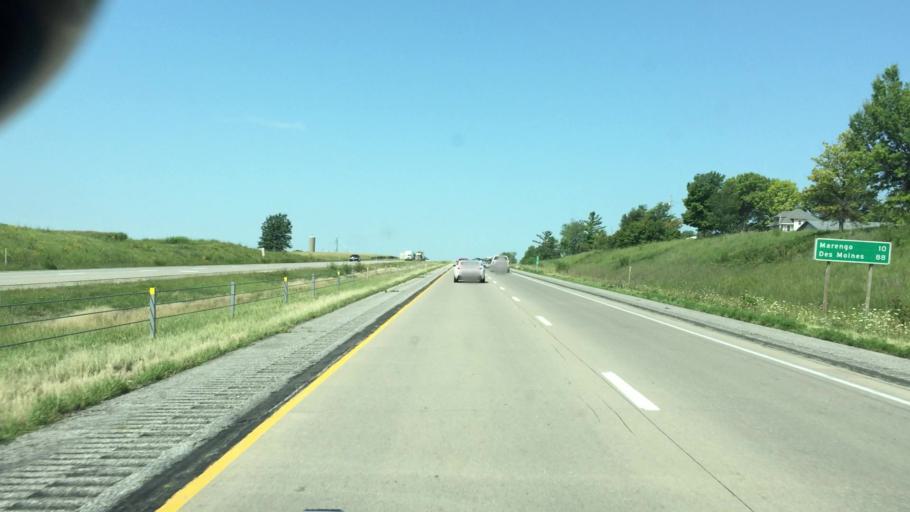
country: US
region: Iowa
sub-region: Iowa County
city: Williamsburg
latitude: 41.6873
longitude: -92.0243
